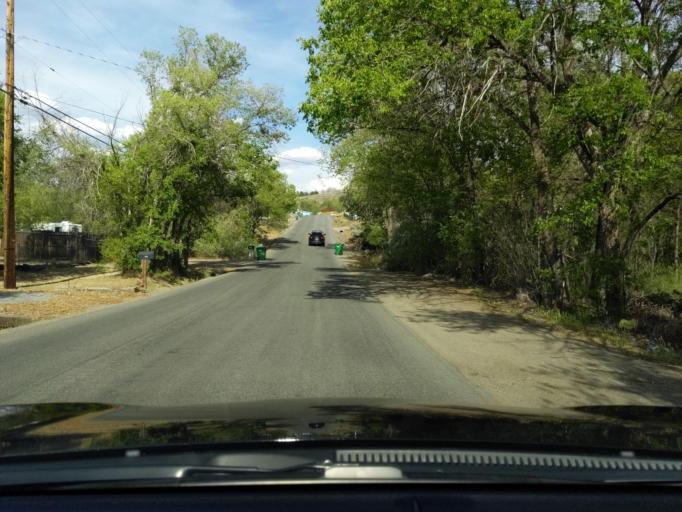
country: US
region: Nevada
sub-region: Washoe County
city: Sun Valley
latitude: 39.5784
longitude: -119.7778
